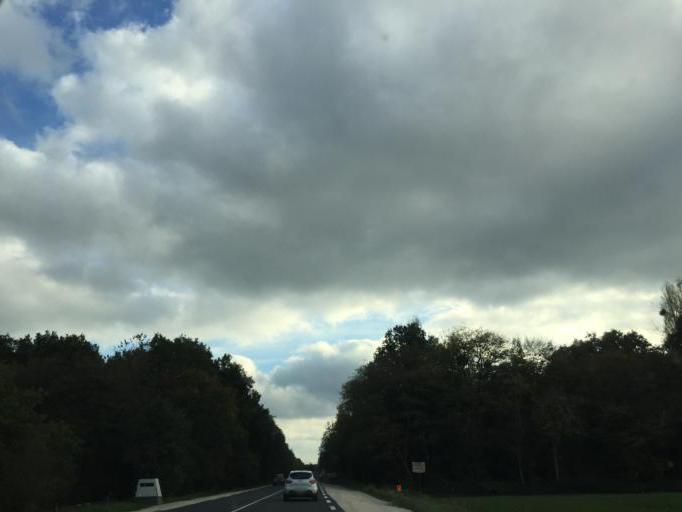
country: FR
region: Ile-de-France
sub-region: Departement de Seine-et-Marne
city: Villeneuve-le-Comte
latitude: 48.8195
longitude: 2.8419
